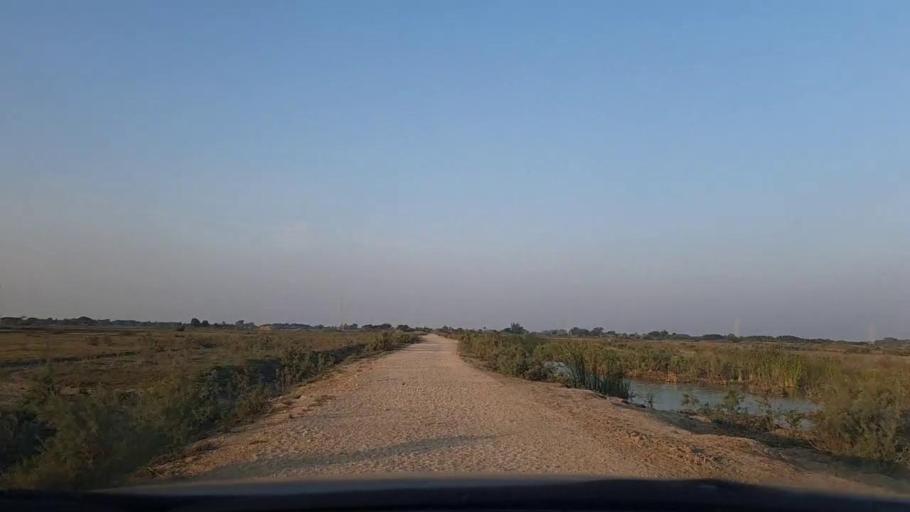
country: PK
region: Sindh
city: Mirpur Sakro
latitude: 24.5564
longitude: 67.6573
